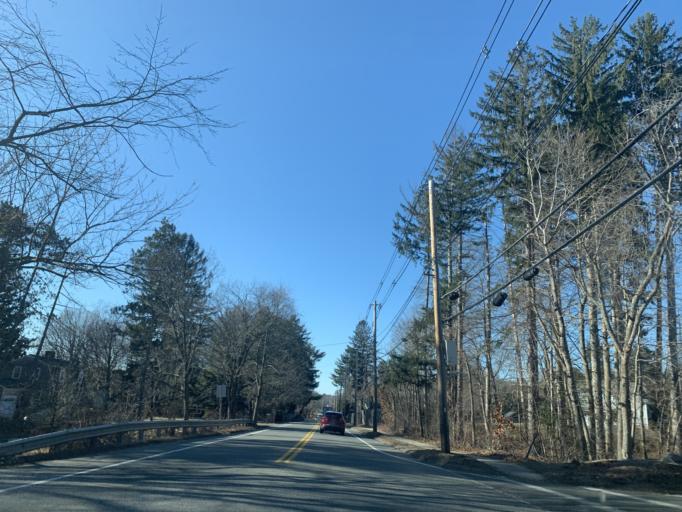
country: US
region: Massachusetts
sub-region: Middlesex County
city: Sudbury
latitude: 42.3614
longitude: -71.4086
